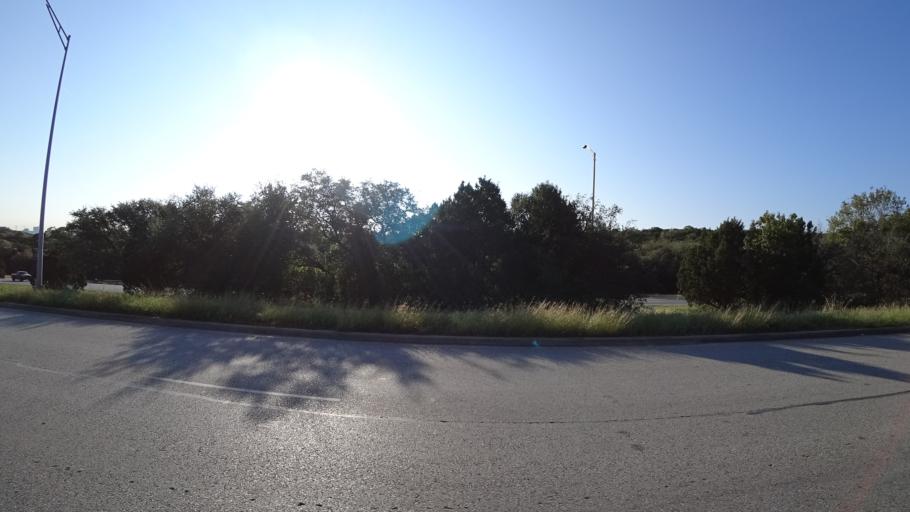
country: US
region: Texas
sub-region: Travis County
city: Rollingwood
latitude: 30.2554
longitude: -97.8039
